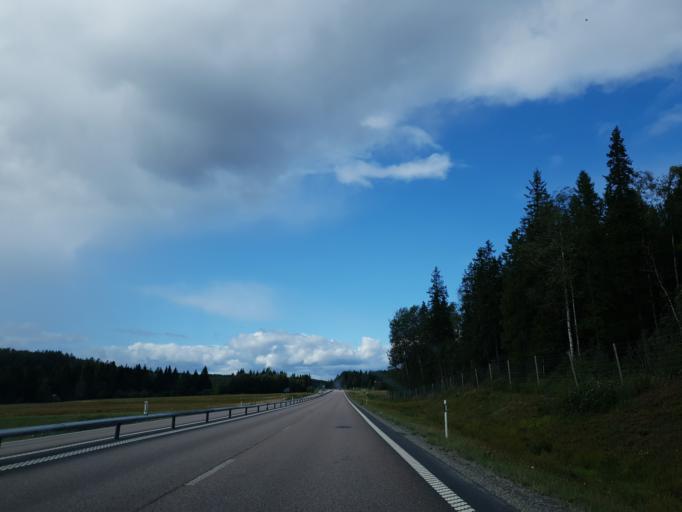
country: SE
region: Vaesternorrland
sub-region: OErnskoeldsviks Kommun
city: Ornskoldsvik
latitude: 63.2991
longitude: 18.8666
